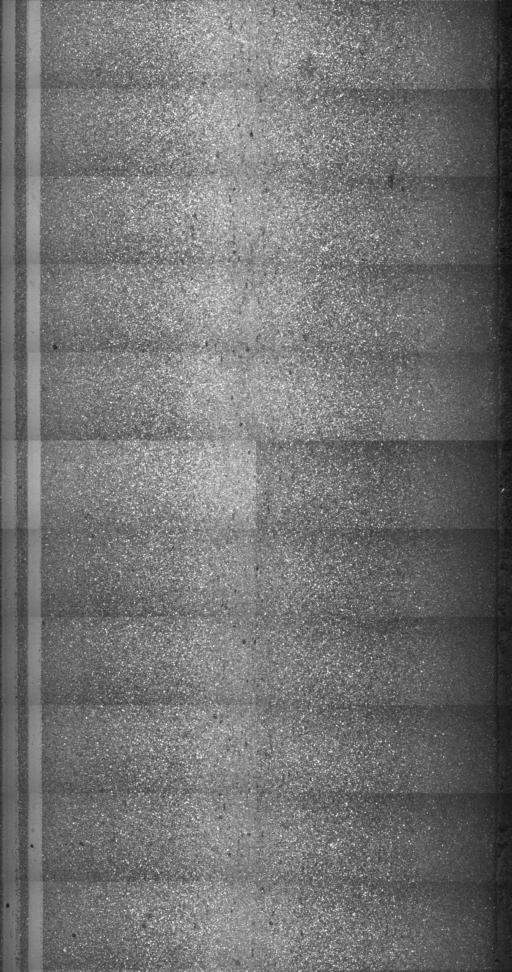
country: US
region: Vermont
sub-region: Addison County
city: Vergennes
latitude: 44.1729
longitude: -73.2472
